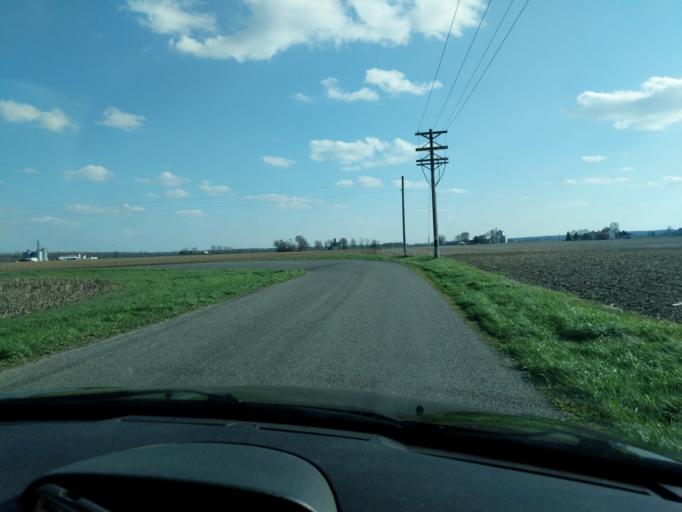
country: US
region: Ohio
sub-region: Champaign County
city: Urbana
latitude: 40.1157
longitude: -83.8085
